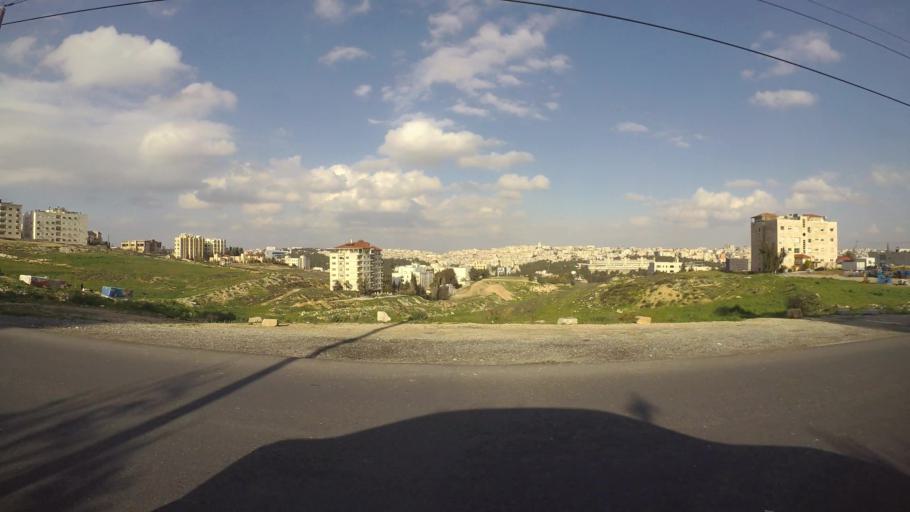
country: JO
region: Amman
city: Al Jubayhah
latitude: 32.0086
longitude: 35.8651
